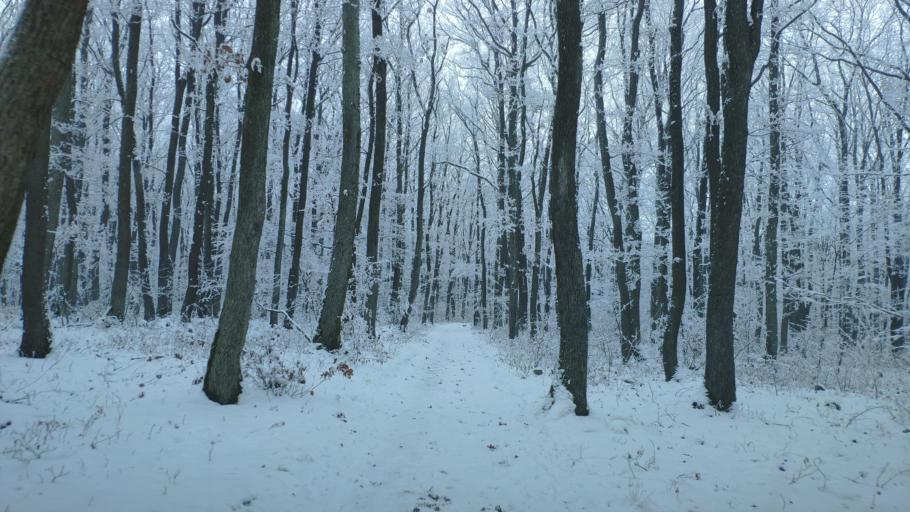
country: SK
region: Kosicky
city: Kosice
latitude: 48.6585
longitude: 21.1852
